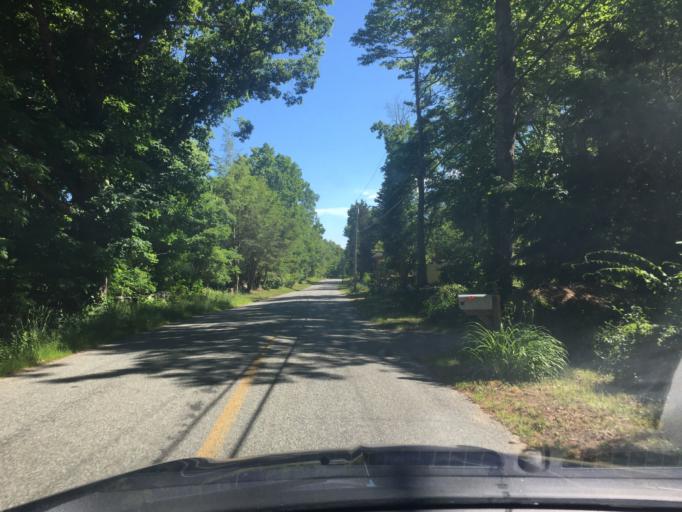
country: US
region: Rhode Island
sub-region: Washington County
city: Hopkinton
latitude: 41.4901
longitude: -71.8093
